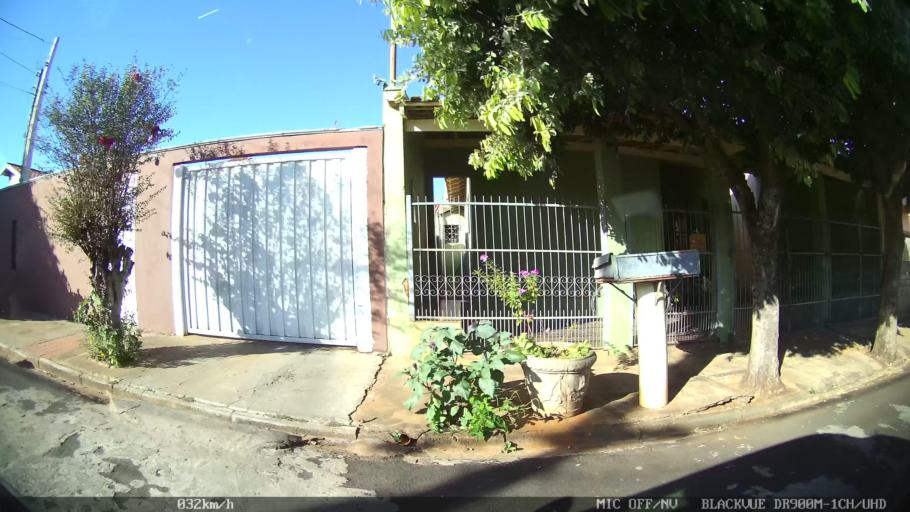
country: BR
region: Sao Paulo
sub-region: Olimpia
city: Olimpia
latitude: -20.7327
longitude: -48.9082
